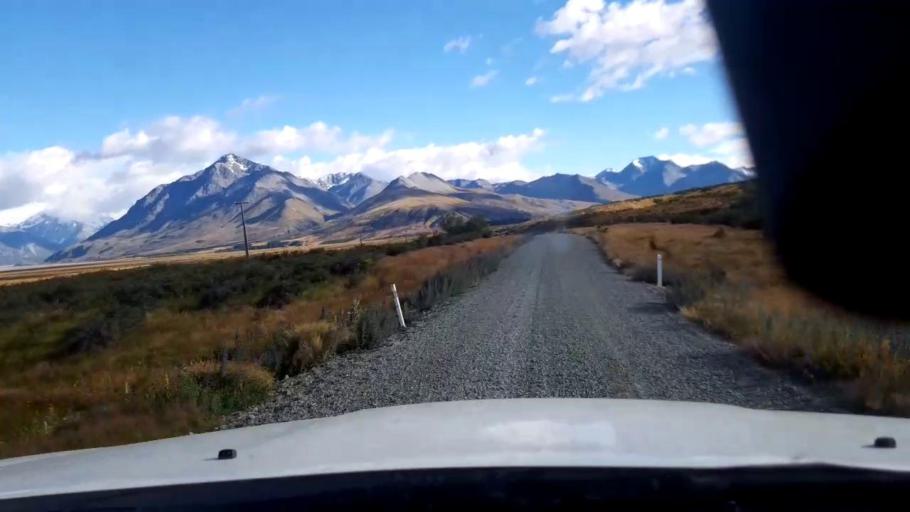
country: NZ
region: Canterbury
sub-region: Timaru District
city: Pleasant Point
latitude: -43.7520
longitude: 170.5708
